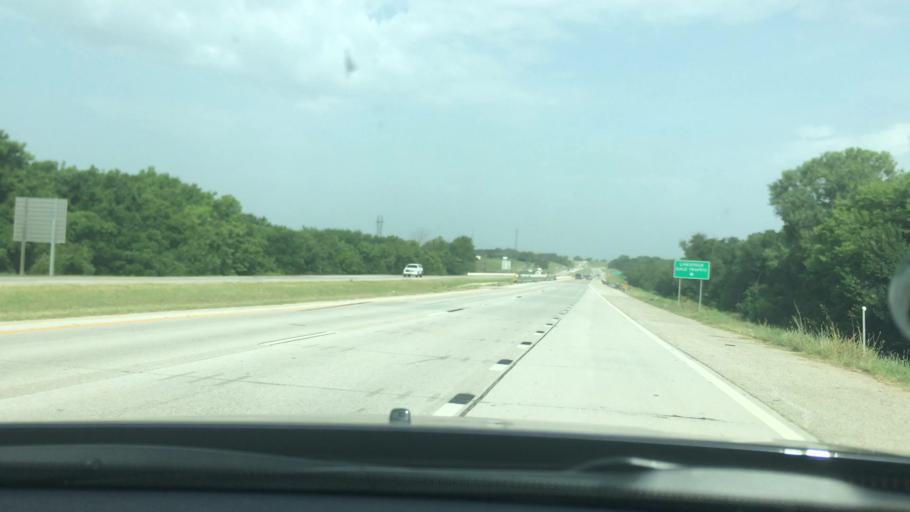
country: US
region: Oklahoma
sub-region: Pontotoc County
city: Ada
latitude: 34.7783
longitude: -96.7070
